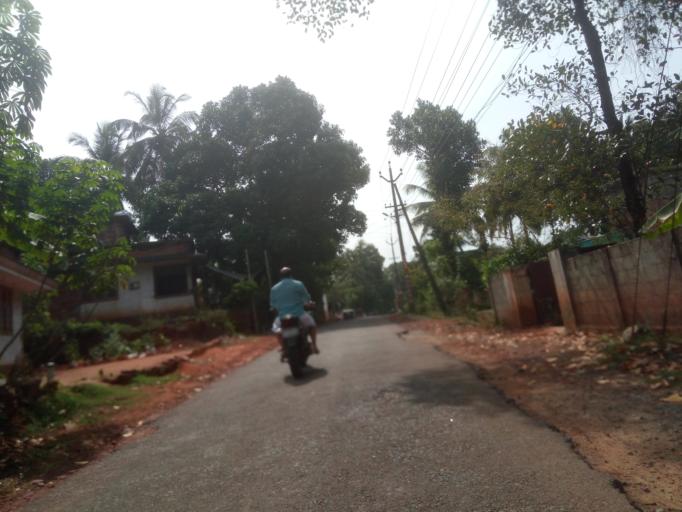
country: IN
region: Kerala
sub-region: Malappuram
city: Ponnani
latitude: 10.7924
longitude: 76.0283
